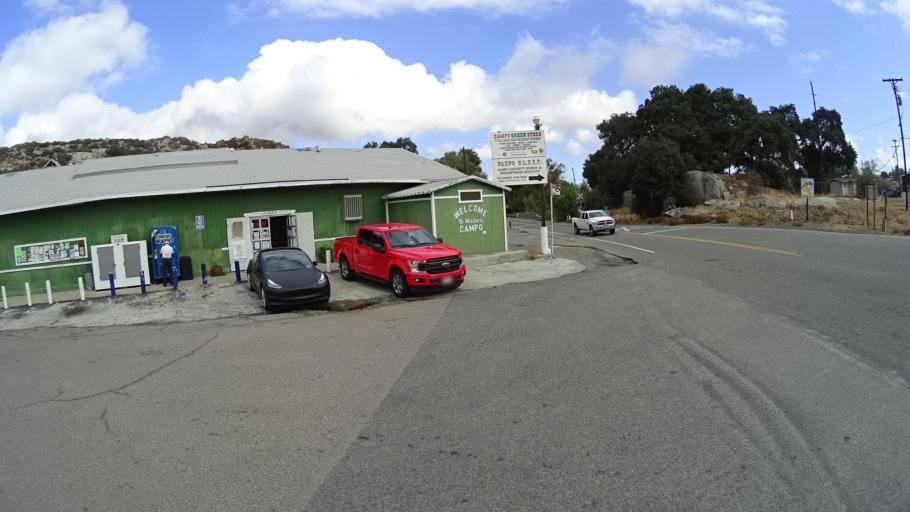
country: US
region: California
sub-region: San Diego County
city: Campo
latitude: 32.6083
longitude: -116.4743
